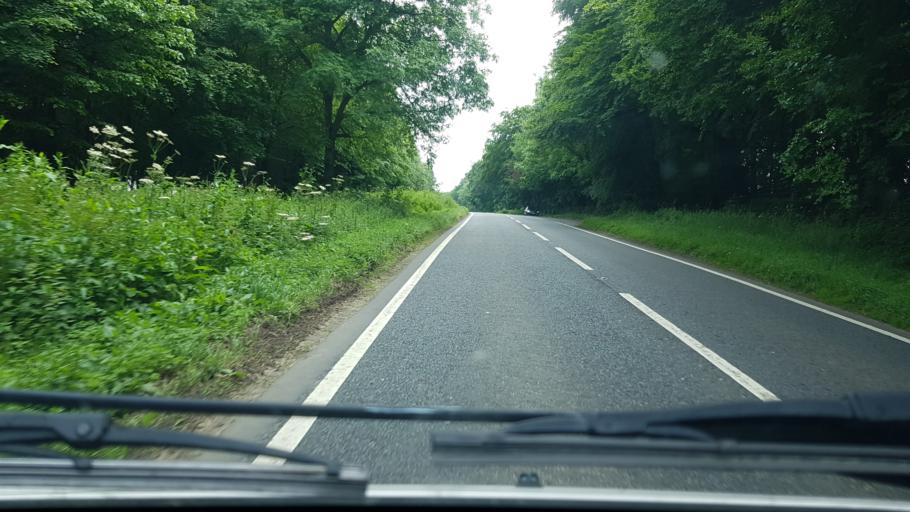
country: GB
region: England
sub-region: Worcestershire
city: Broadway
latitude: 52.0272
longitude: -1.8213
